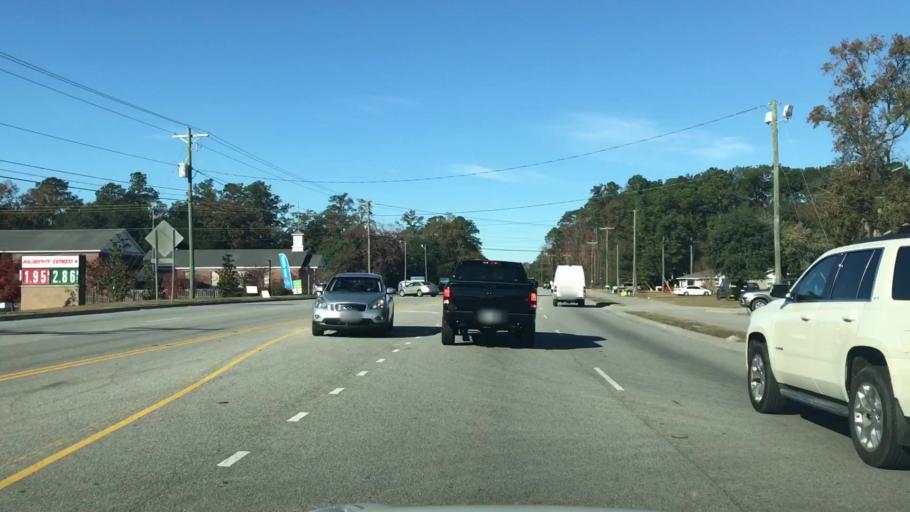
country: US
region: South Carolina
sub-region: Dorchester County
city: Centerville
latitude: 32.9685
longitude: -80.2036
